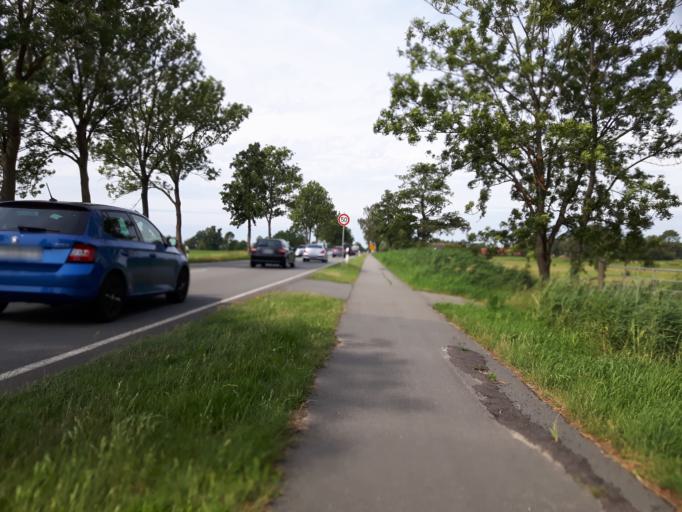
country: DE
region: Lower Saxony
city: Ovelgonne
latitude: 53.2673
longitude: 8.3433
